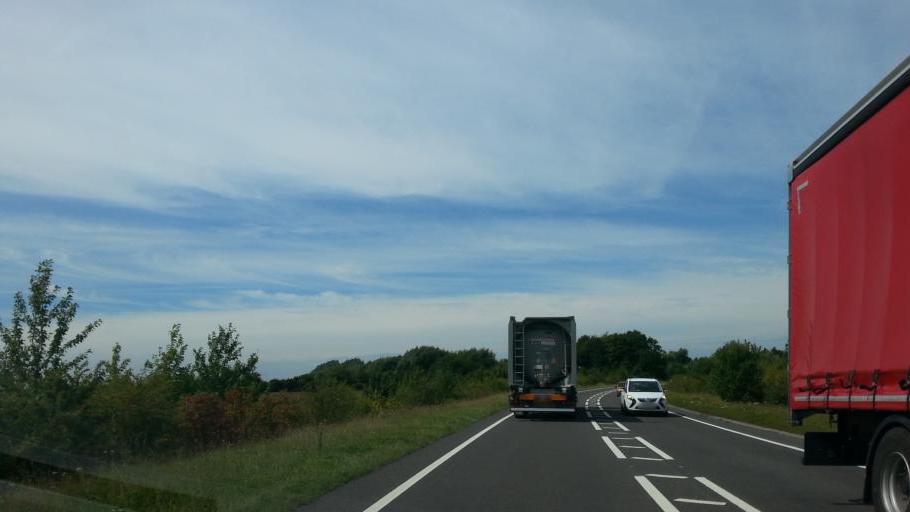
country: GB
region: England
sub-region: Suffolk
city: Exning
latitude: 52.2956
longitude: 0.3828
